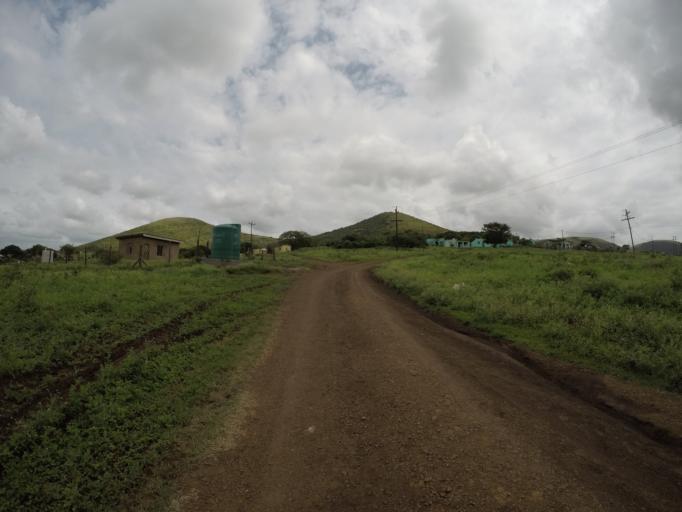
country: ZA
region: KwaZulu-Natal
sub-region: uThungulu District Municipality
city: Empangeni
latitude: -28.5902
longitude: 31.8887
